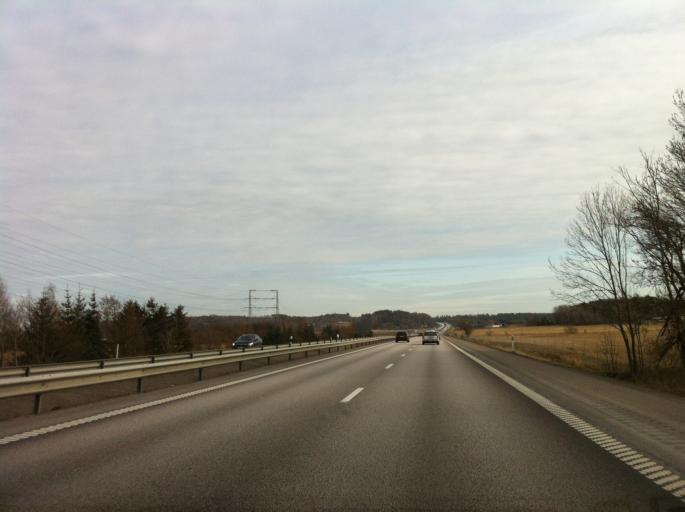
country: SE
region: Vaestra Goetaland
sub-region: Molndal
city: Lindome
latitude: 57.5388
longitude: 12.0515
